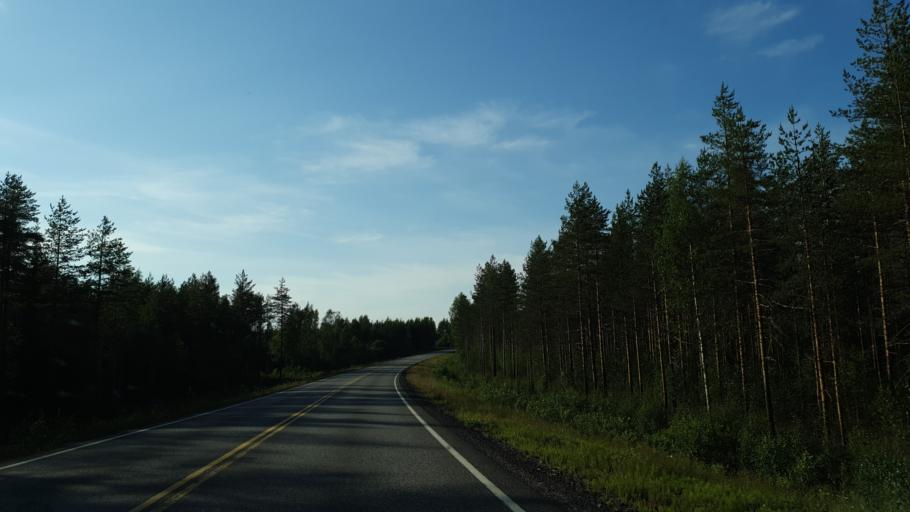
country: FI
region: Kainuu
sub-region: Kehys-Kainuu
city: Kuhmo
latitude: 64.0775
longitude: 29.4886
